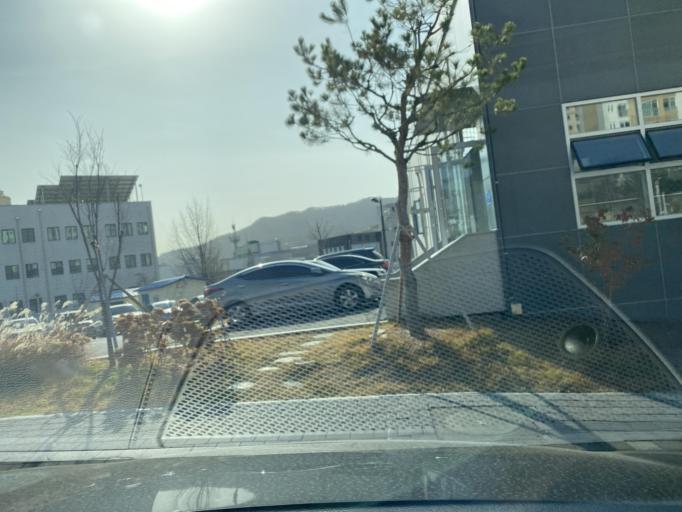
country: KR
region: Chungcheongnam-do
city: Yesan
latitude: 36.6811
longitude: 126.8466
